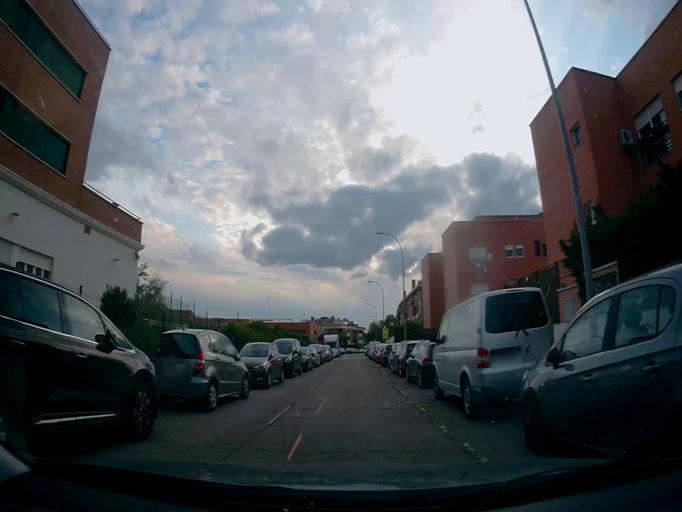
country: ES
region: Madrid
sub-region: Provincia de Madrid
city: Alcorcon
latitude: 40.3362
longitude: -3.8284
